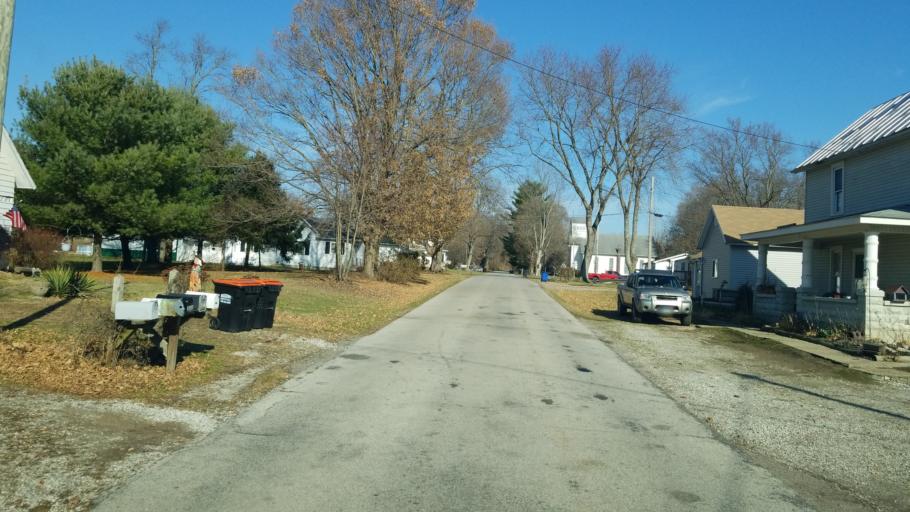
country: US
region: Ohio
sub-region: Licking County
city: Utica
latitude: 40.1585
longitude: -82.4533
